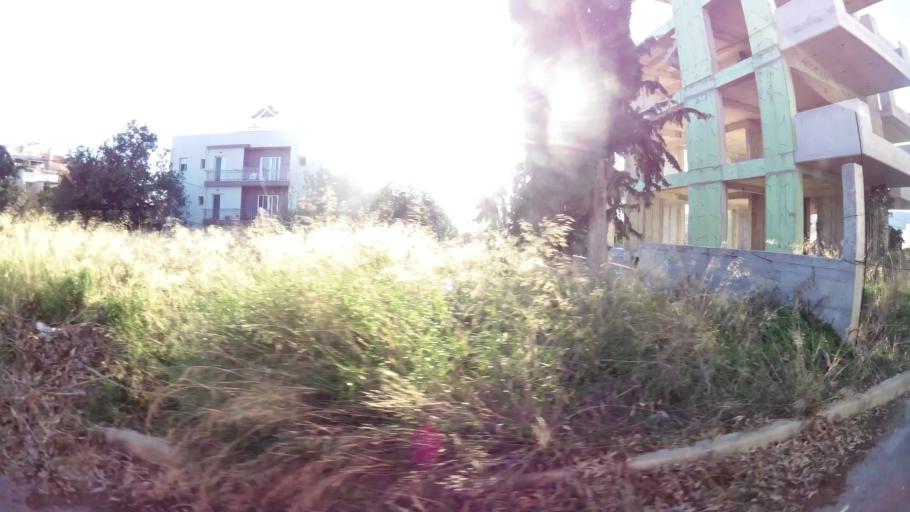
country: GR
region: Attica
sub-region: Nomarchia Anatolikis Attikis
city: Rafina
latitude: 38.0203
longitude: 24.0030
